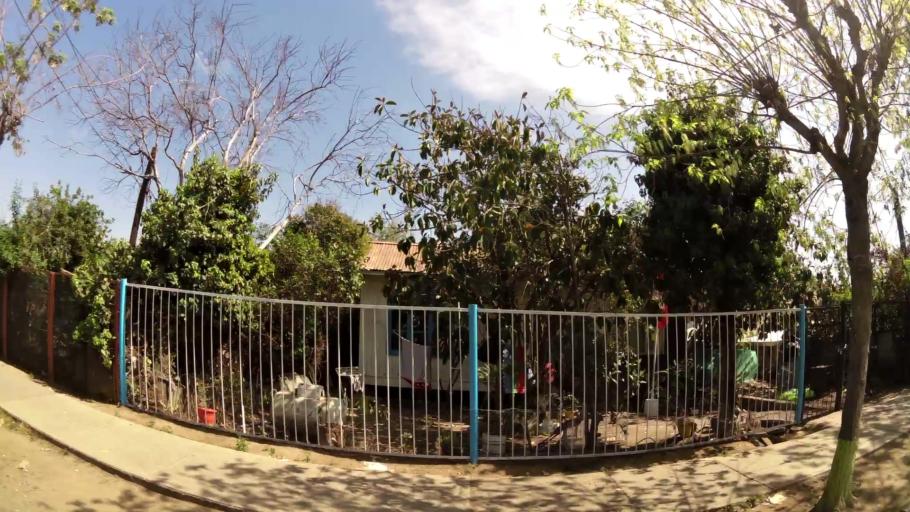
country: CL
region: Santiago Metropolitan
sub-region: Provincia de Santiago
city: Villa Presidente Frei, Nunoa, Santiago, Chile
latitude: -33.4717
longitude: -70.5386
